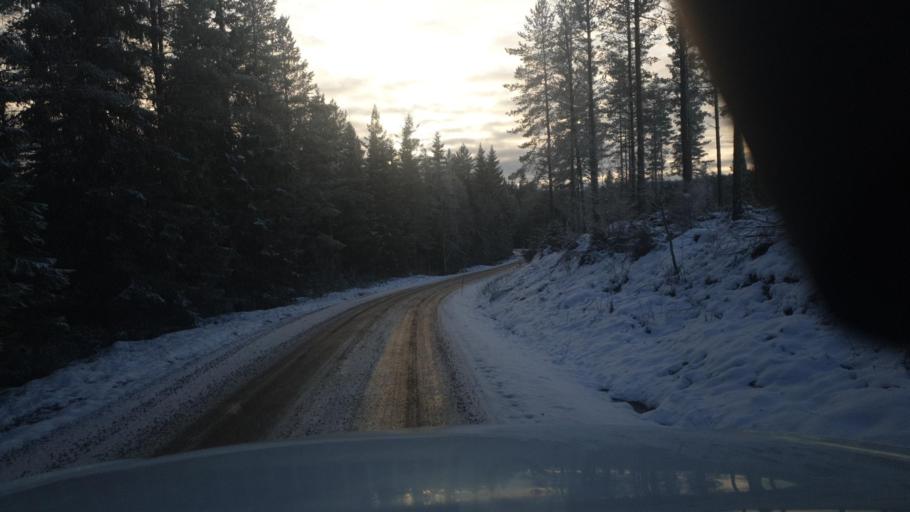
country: SE
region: Vaermland
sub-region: Arvika Kommun
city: Arvika
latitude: 59.9868
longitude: 12.6616
